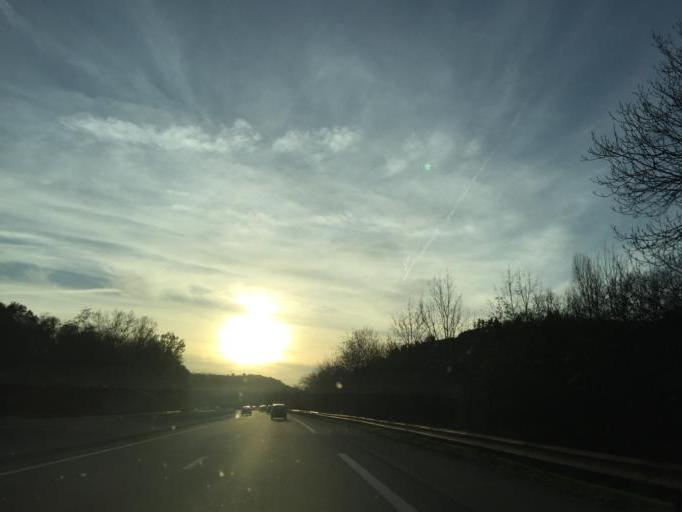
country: FR
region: Rhone-Alpes
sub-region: Departement du Rhone
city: Echalas
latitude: 45.5488
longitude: 4.6748
